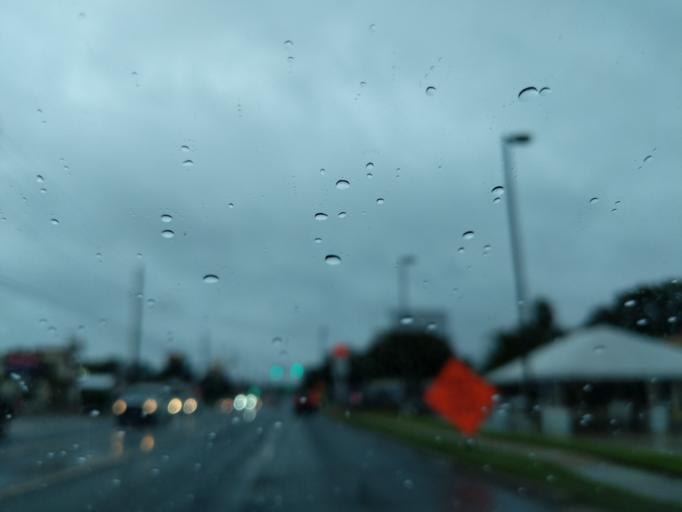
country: US
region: Texas
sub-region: Nacogdoches County
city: Nacogdoches
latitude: 31.6290
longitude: -94.6525
